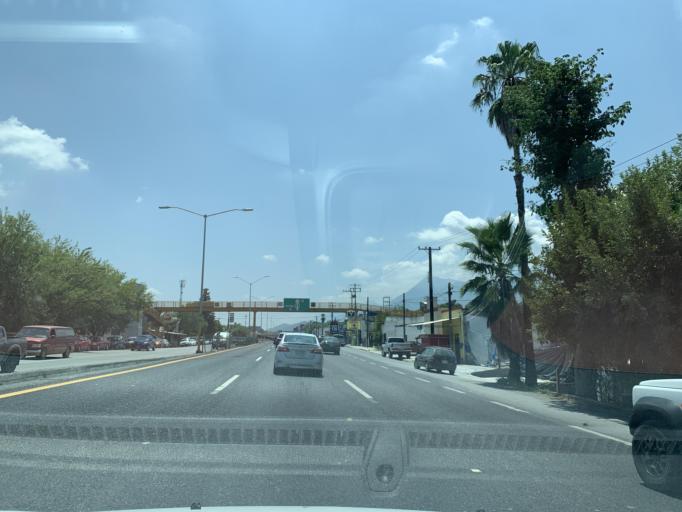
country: MX
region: Nuevo Leon
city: Santiago
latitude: 25.4081
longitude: -100.1355
